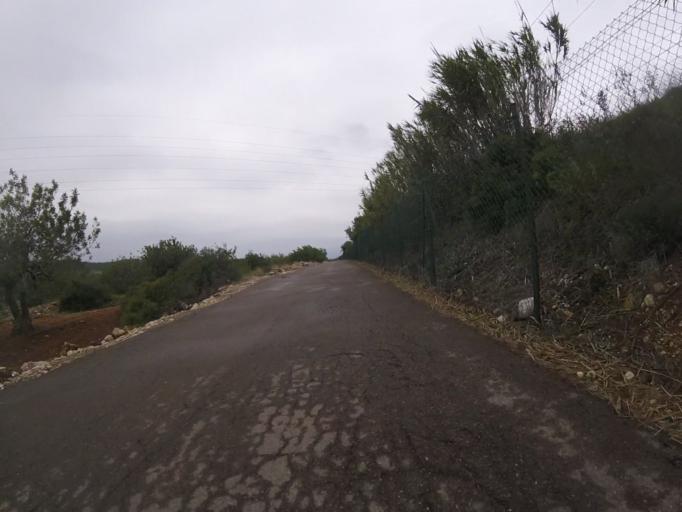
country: ES
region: Valencia
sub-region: Provincia de Castello
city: Alcala de Xivert
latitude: 40.2739
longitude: 0.2401
